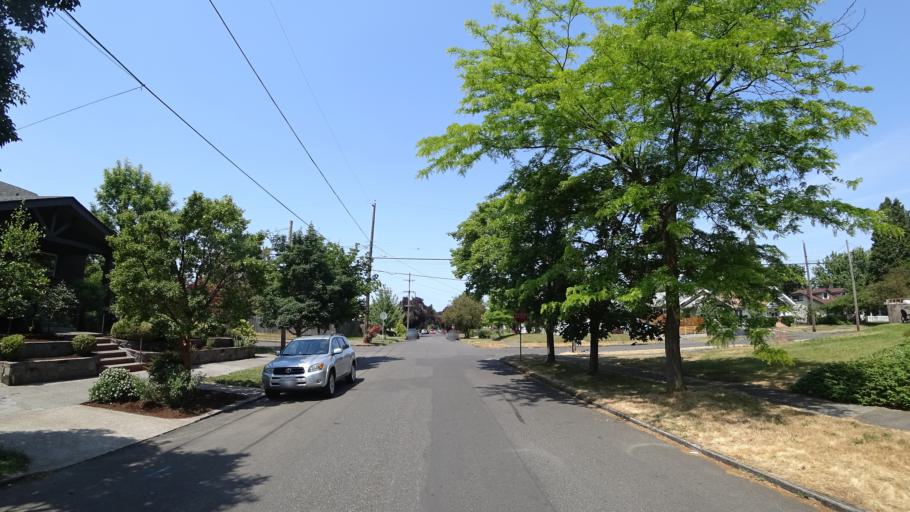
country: US
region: Oregon
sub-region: Multnomah County
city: Portland
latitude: 45.5785
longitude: -122.6890
